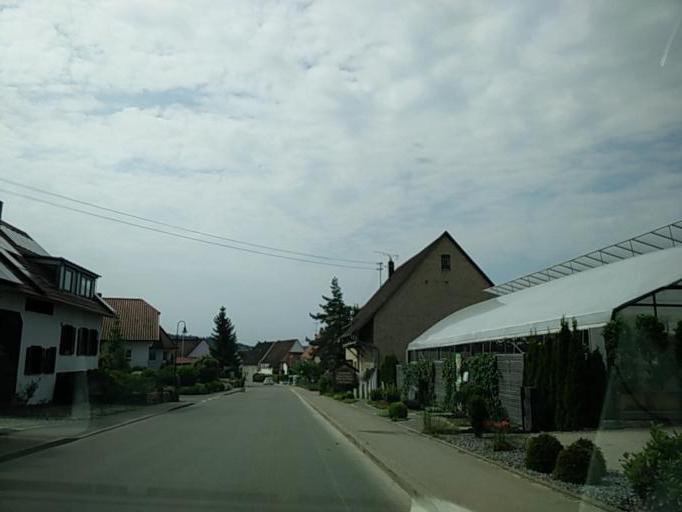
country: DE
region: Baden-Wuerttemberg
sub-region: Tuebingen Region
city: Hirrlingen
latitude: 48.4146
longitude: 8.8868
